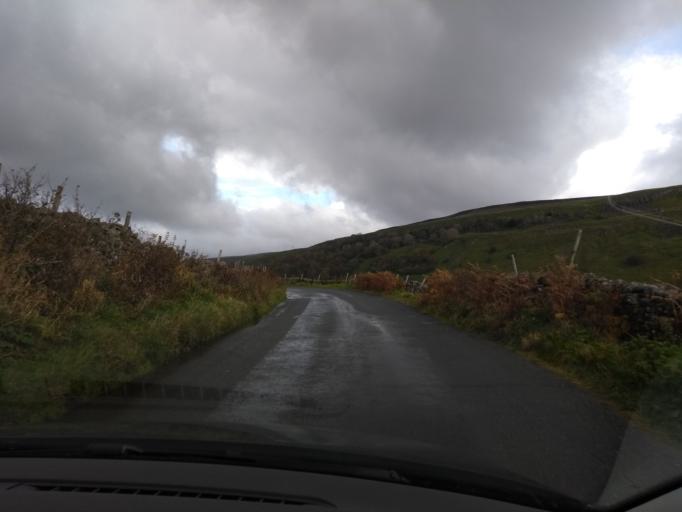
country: GB
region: England
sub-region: Cumbria
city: Kirkby Stephen
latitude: 54.3895
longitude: -2.1731
